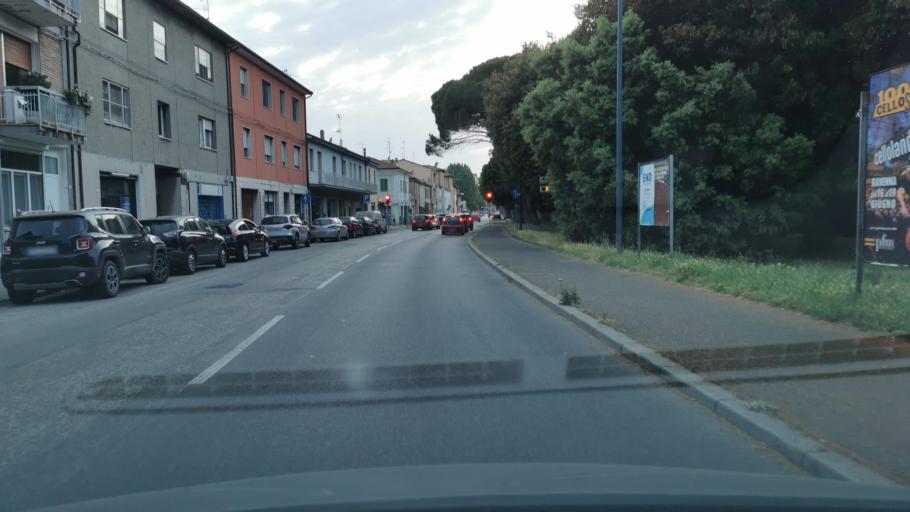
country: IT
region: Emilia-Romagna
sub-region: Provincia di Ravenna
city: Ravenna
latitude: 44.4130
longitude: 12.1931
